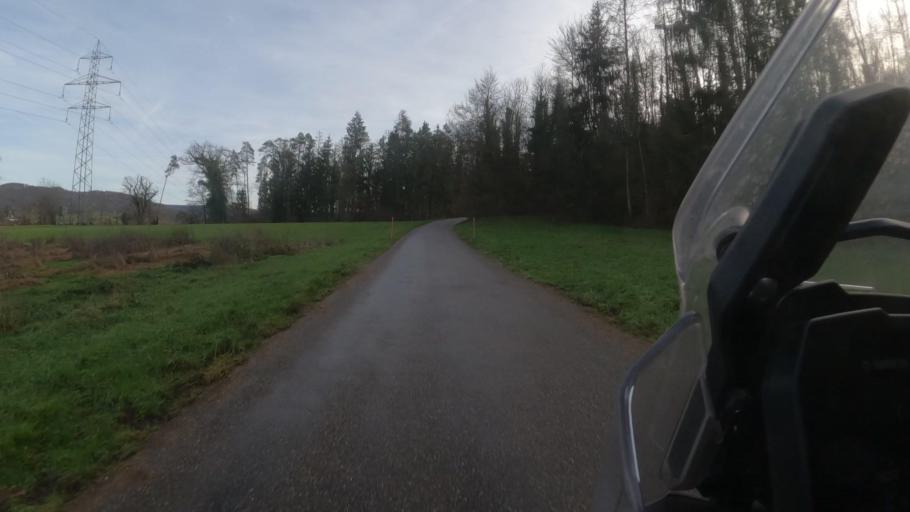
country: CH
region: Zurich
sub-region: Bezirk Buelach
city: Glattfelden
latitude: 47.5530
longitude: 8.4998
